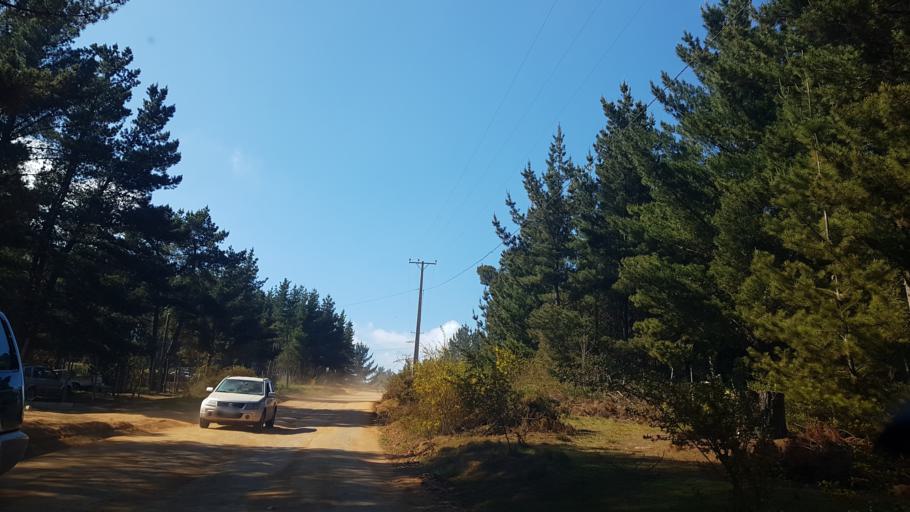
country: CL
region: Valparaiso
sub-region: Provincia de Valparaiso
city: Valparaiso
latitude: -33.1315
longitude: -71.6642
